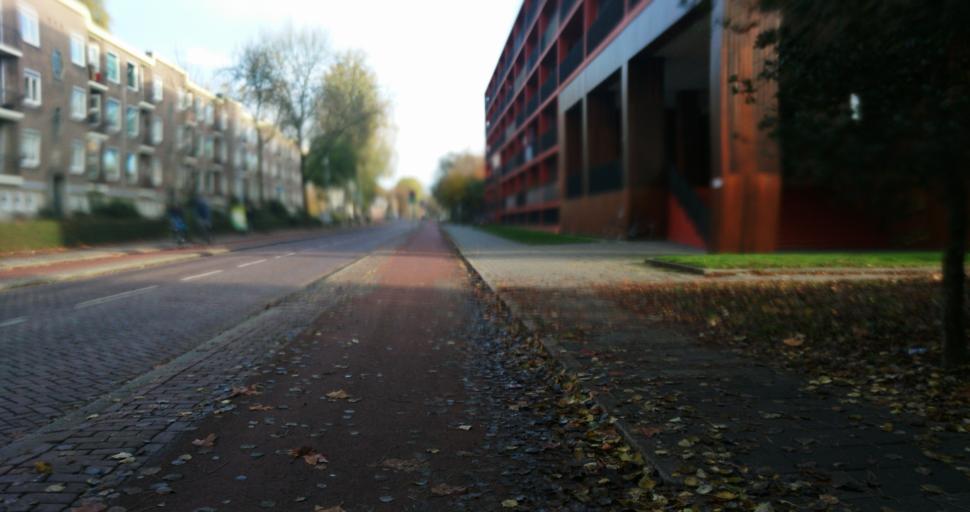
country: NL
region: Groningen
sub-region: Gemeente Groningen
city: Korrewegwijk
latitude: 53.2342
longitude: 6.5769
